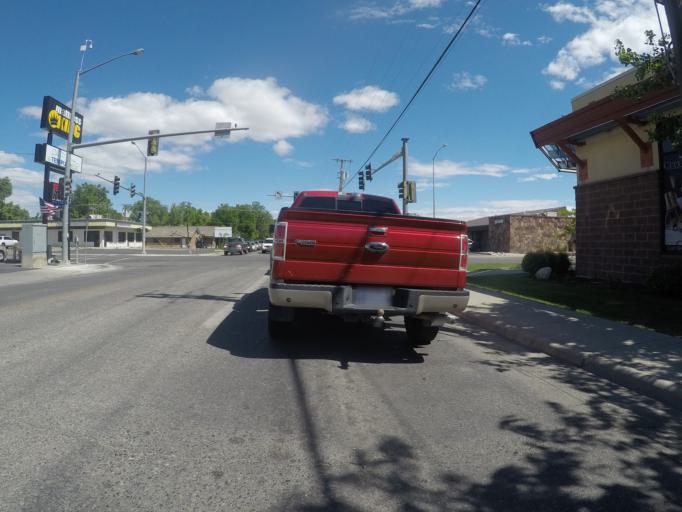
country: US
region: Montana
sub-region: Yellowstone County
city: Billings
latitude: 45.7838
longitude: -108.5590
